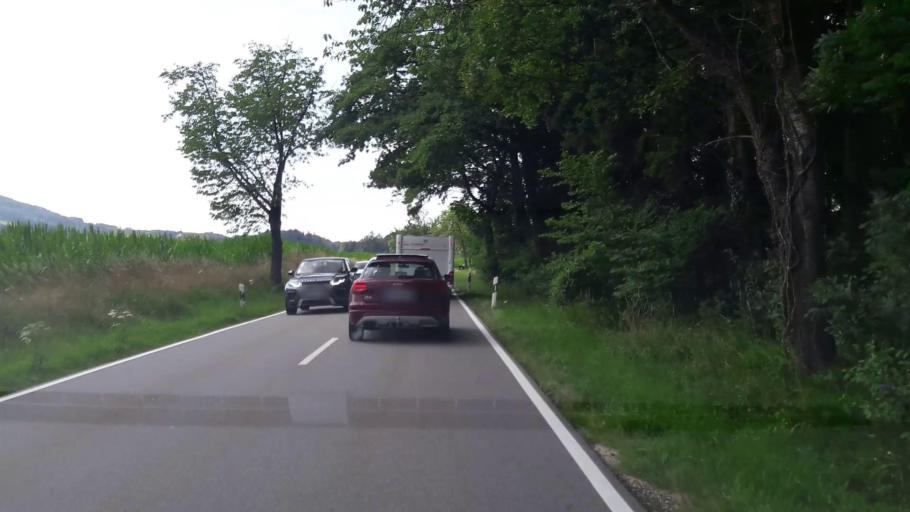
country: DE
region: Bavaria
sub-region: Upper Bavaria
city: Anger
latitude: 47.8116
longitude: 12.8570
